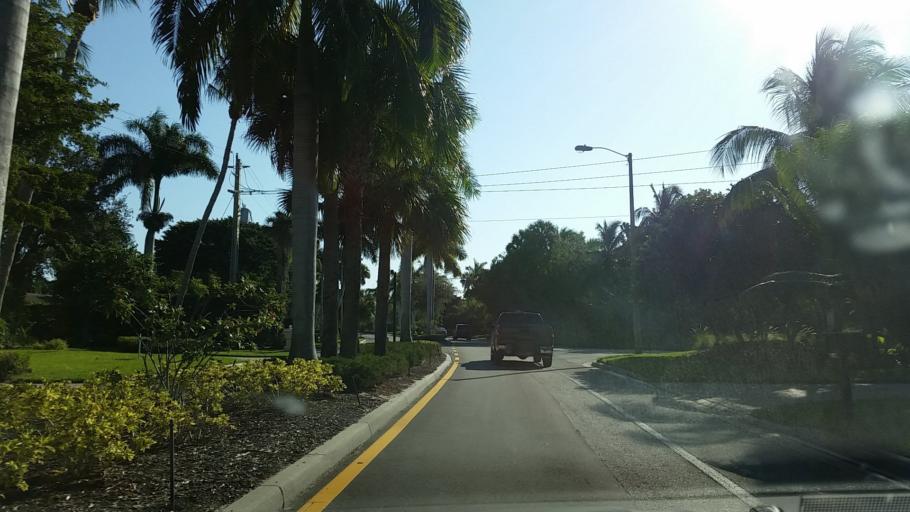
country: US
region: Florida
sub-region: Collier County
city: Naples
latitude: 26.1726
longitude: -81.8076
